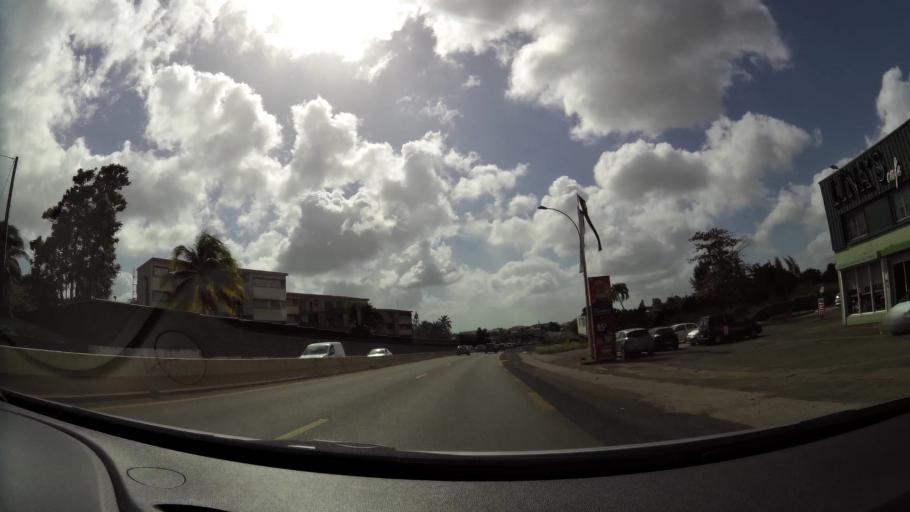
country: MQ
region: Martinique
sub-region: Martinique
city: Le Lamentin
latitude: 14.6212
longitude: -60.9918
